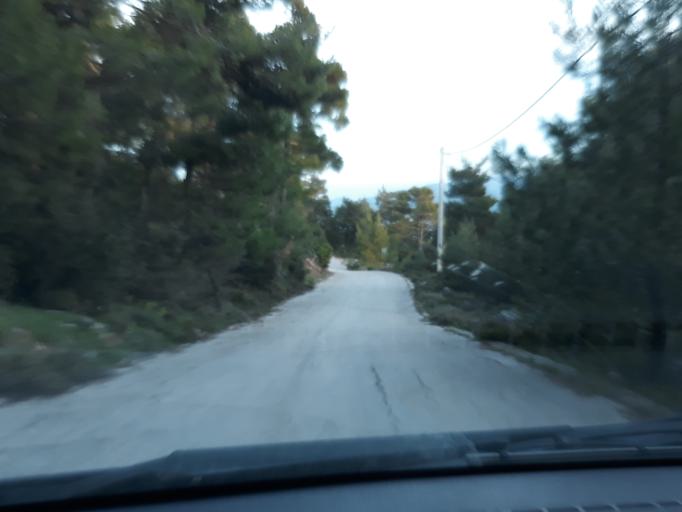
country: GR
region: Attica
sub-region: Nomarchia Anatolikis Attikis
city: Afidnes
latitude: 38.2140
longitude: 23.8099
